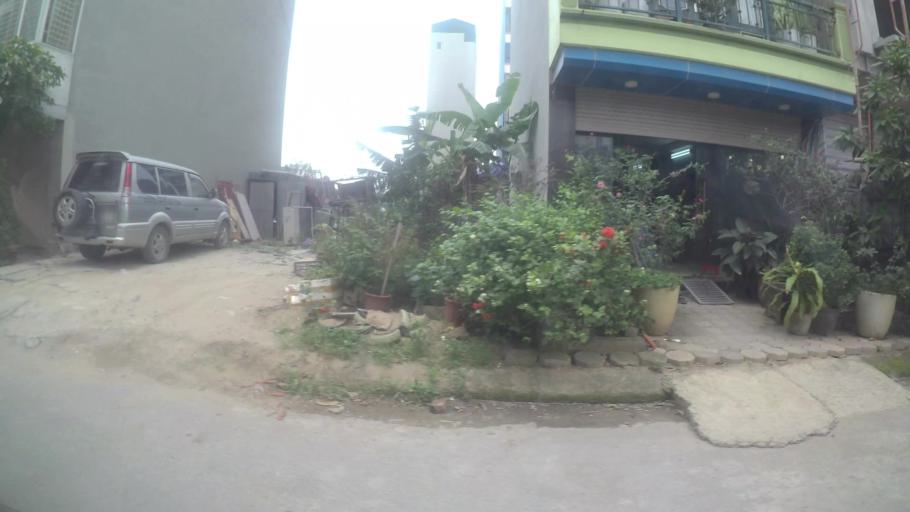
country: VN
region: Ha Noi
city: Ha Dong
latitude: 20.9809
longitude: 105.7705
